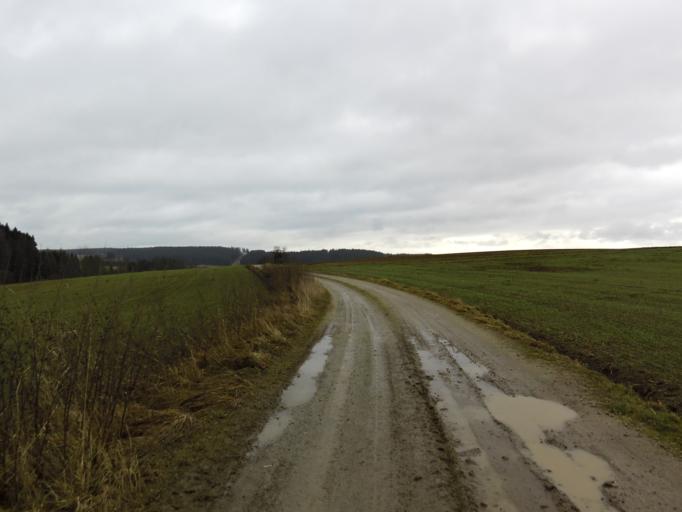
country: DE
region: Bavaria
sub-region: Upper Franconia
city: Wunsiedel
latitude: 50.0633
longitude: 12.0363
